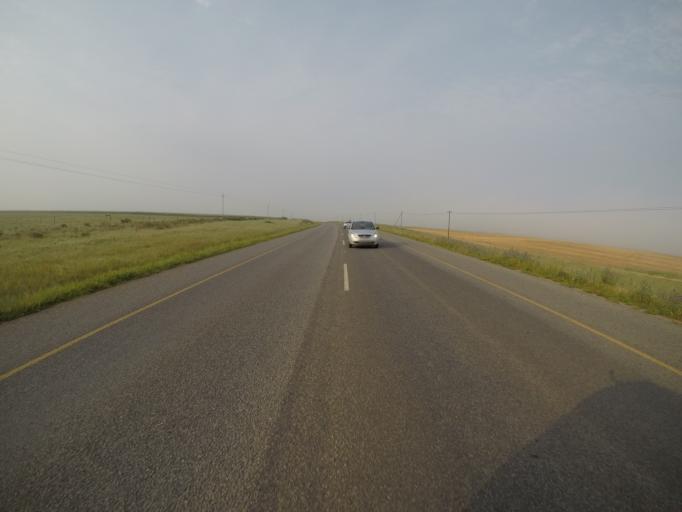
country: ZA
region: Western Cape
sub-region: West Coast District Municipality
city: Malmesbury
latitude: -33.6530
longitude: 18.7095
